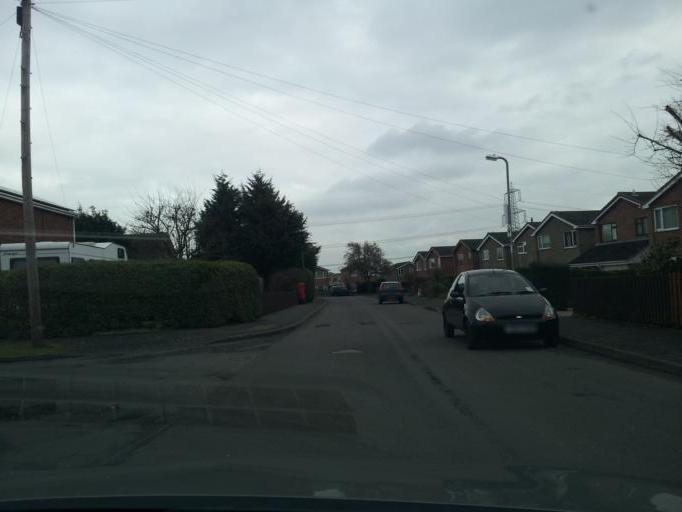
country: GB
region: England
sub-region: Lincolnshire
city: Barrowby
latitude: 52.9133
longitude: -0.6846
